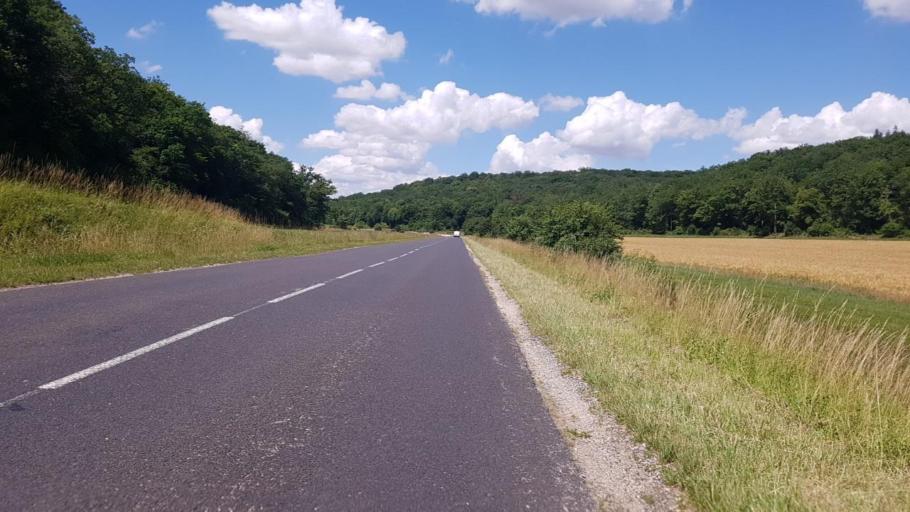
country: FR
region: Lorraine
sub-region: Departement de la Meuse
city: Vacon
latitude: 48.6724
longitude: 5.5944
